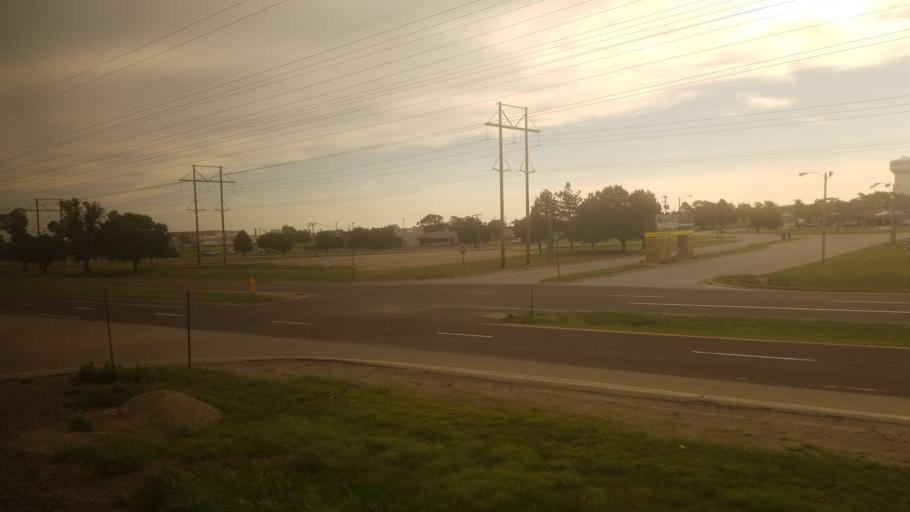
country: US
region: Kansas
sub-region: Shawnee County
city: Topeka
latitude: 38.9463
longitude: -95.6876
